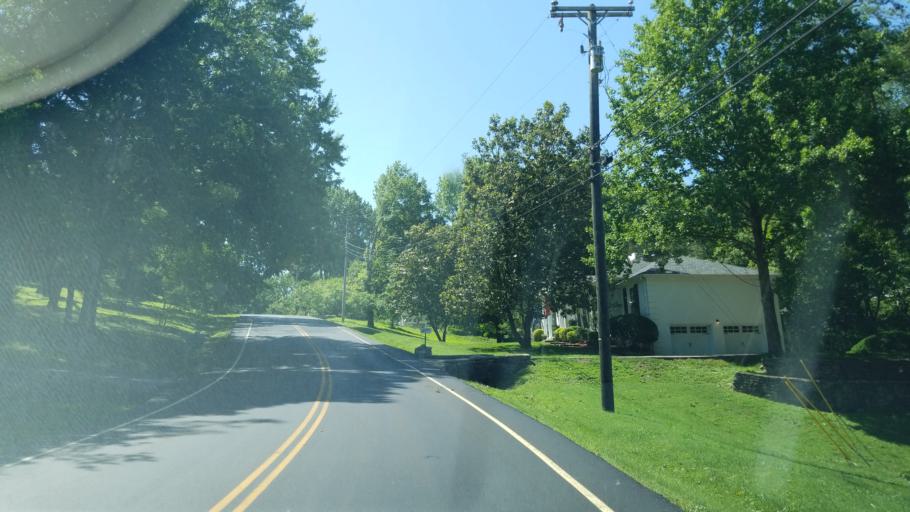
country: US
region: Tennessee
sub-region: Davidson County
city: Forest Hills
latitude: 36.0608
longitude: -86.8191
